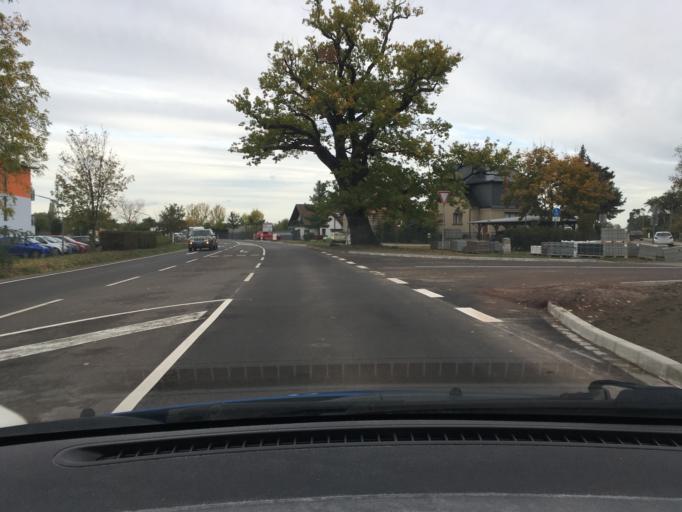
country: DE
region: Saxony-Anhalt
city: Wahlitz
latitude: 52.1070
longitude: 11.7814
